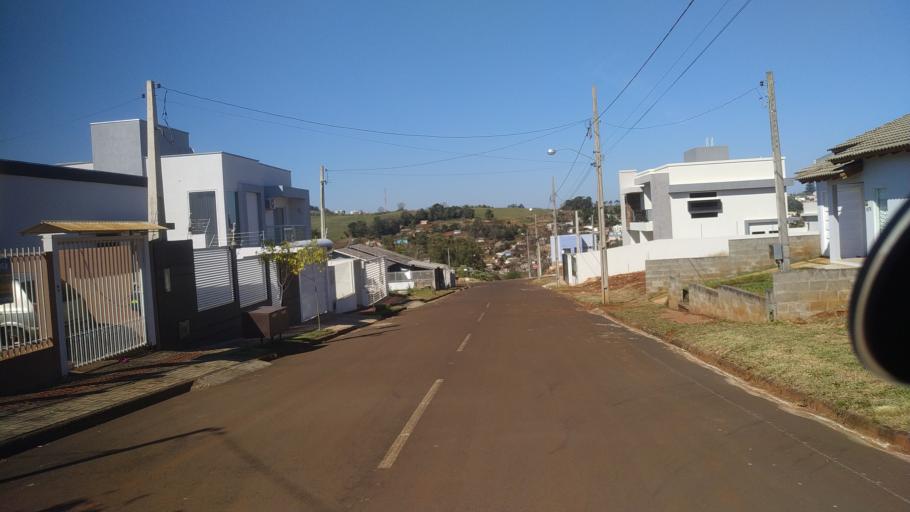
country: BR
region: Santa Catarina
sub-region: Chapeco
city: Chapeco
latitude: -27.0903
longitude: -52.5803
